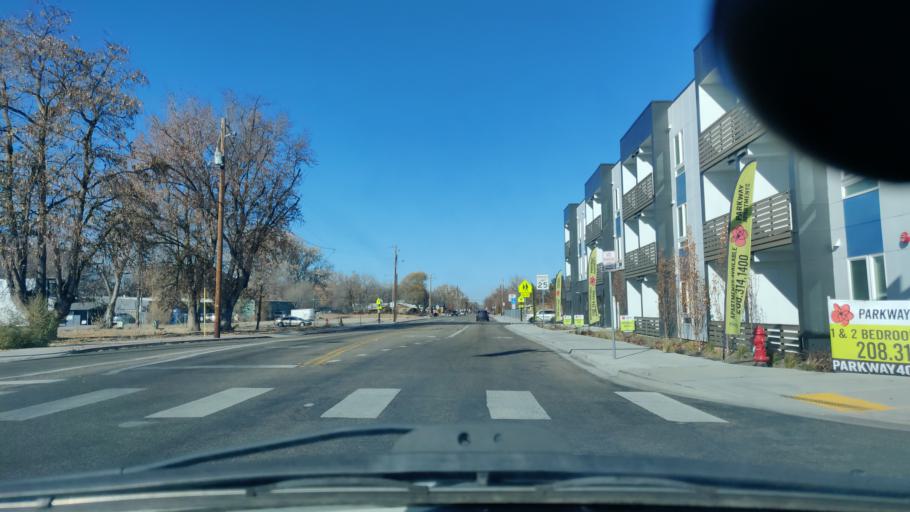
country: US
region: Idaho
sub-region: Ada County
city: Garden City
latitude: 43.6340
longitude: -116.2462
